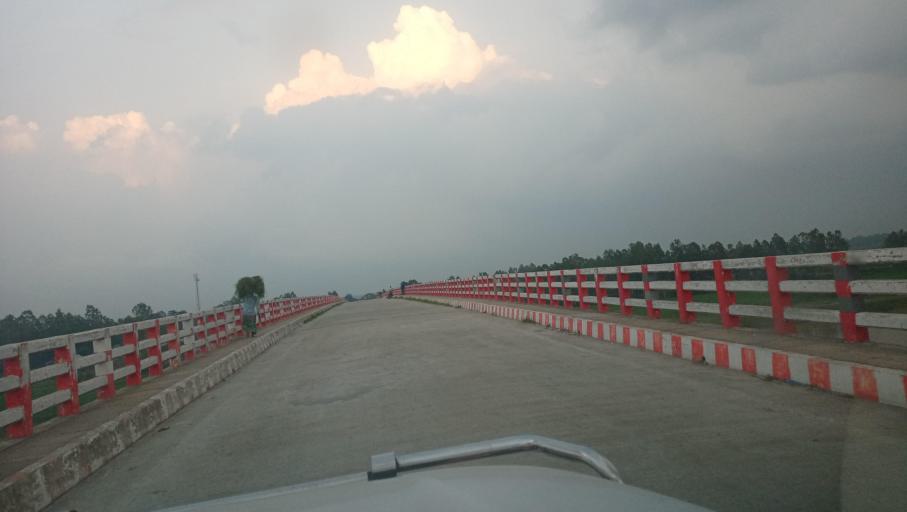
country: BD
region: Dhaka
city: Sherpur
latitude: 25.1766
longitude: 89.7908
